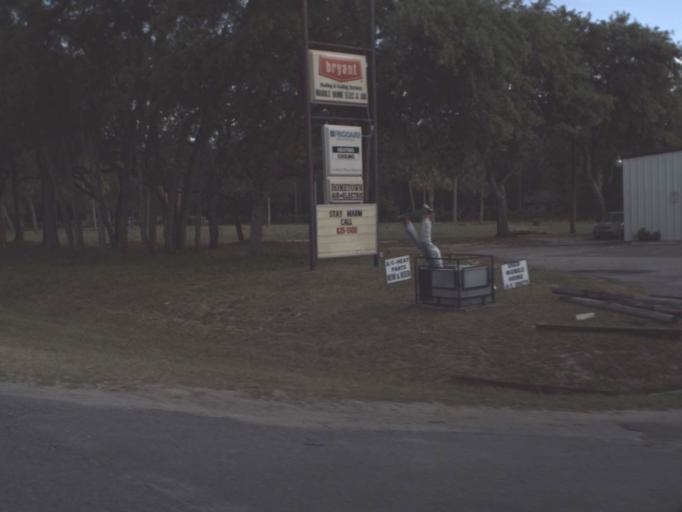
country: US
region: Florida
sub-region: Marion County
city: Silver Springs Shores
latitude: 29.2096
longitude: -81.9474
